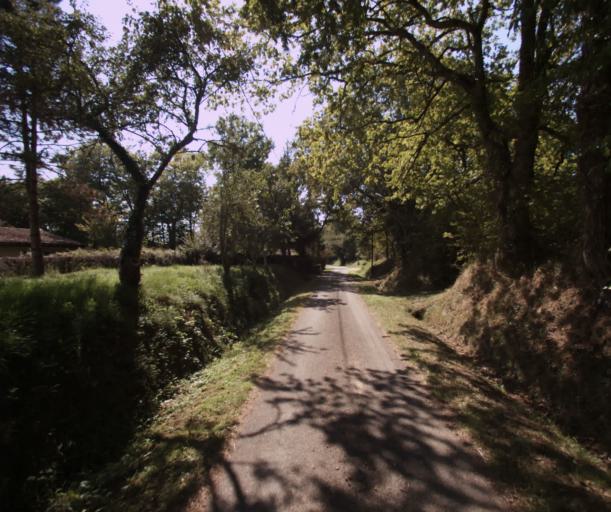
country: FR
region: Midi-Pyrenees
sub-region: Departement du Gers
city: Cazaubon
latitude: 43.9523
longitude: -0.0585
